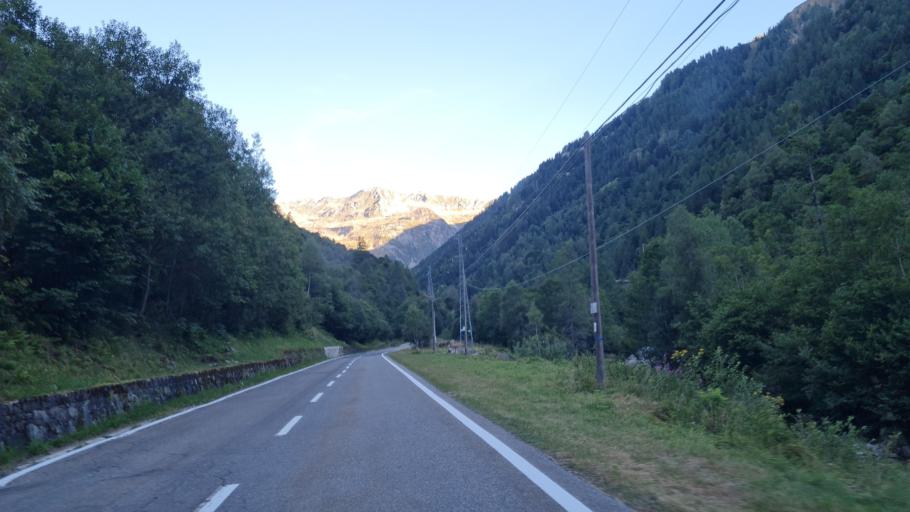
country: IT
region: Piedmont
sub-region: Provincia di Vercelli
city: Rima
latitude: 45.8735
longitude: 8.0183
